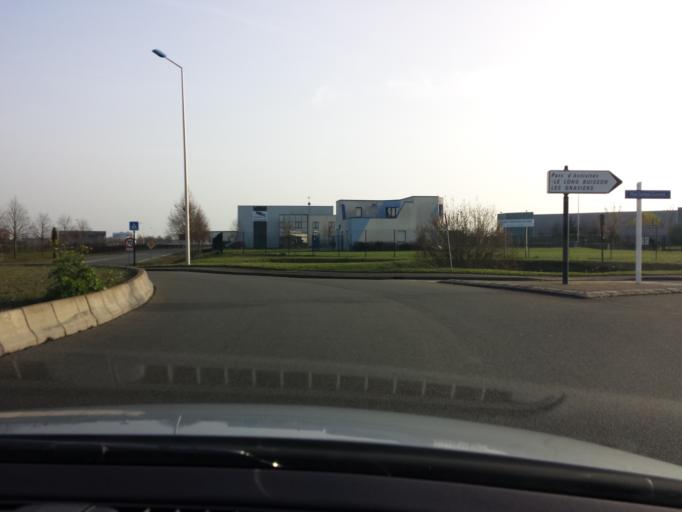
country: FR
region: Haute-Normandie
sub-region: Departement de l'Eure
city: Evreux
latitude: 49.0037
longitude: 1.1766
